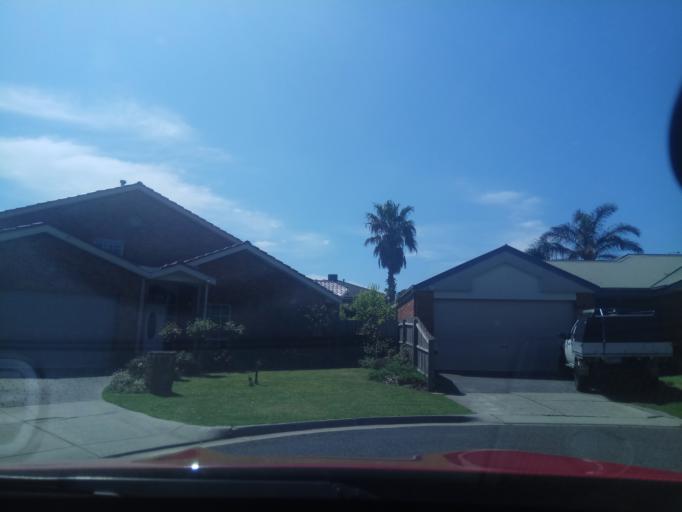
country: AU
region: Victoria
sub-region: Kingston
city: Aspendale Gardens
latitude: -38.0241
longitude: 145.1179
